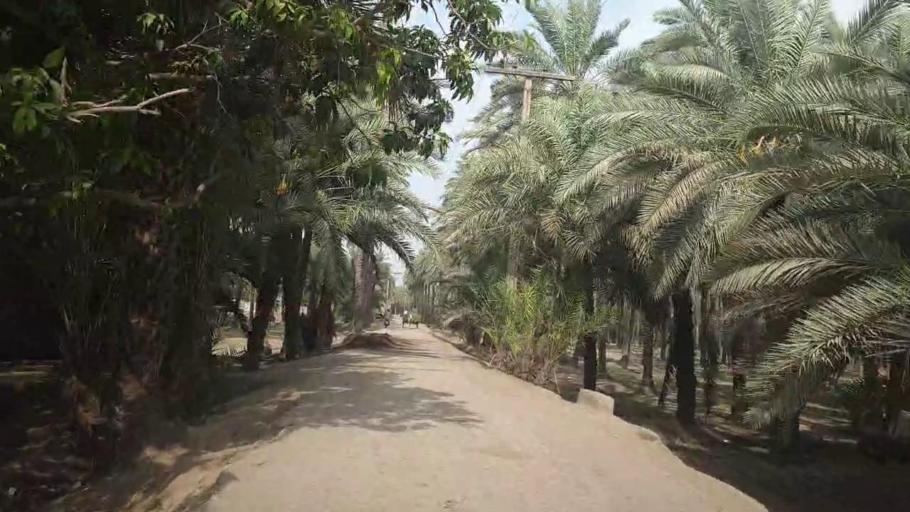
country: PK
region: Sindh
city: Sukkur
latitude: 27.6414
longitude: 68.8053
